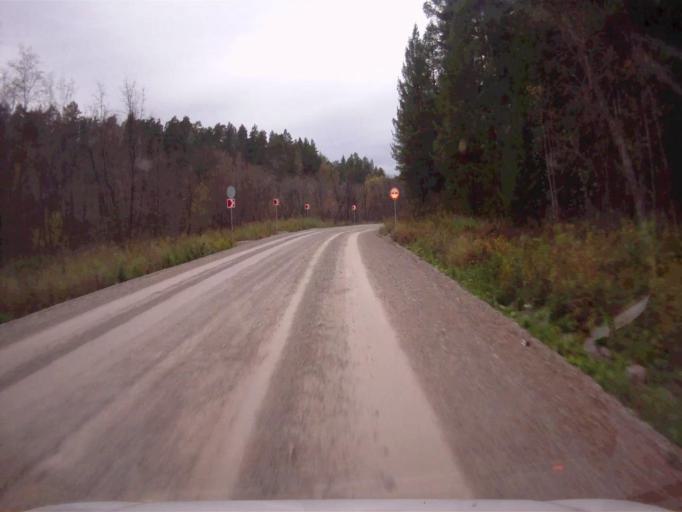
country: RU
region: Chelyabinsk
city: Nyazepetrovsk
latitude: 56.0459
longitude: 59.5035
